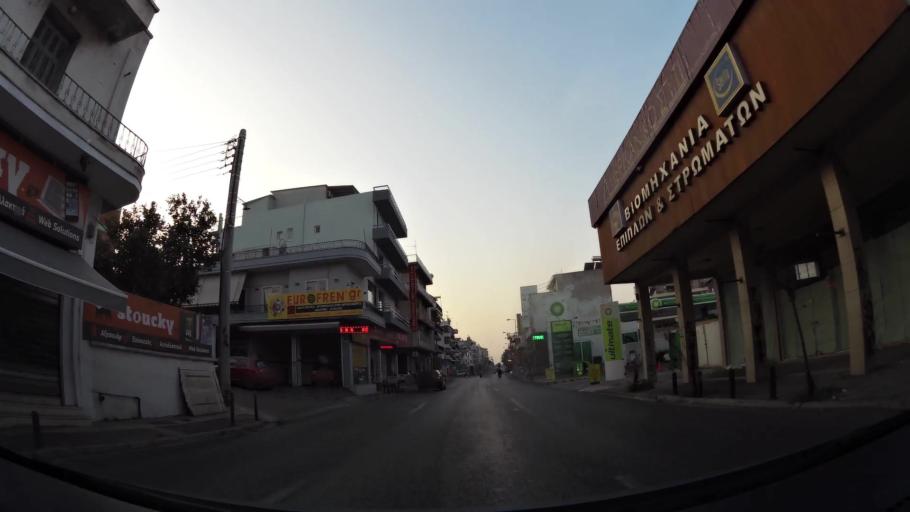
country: GR
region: Attica
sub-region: Nomarchia Athinas
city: Dhafni
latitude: 37.9483
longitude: 23.7385
